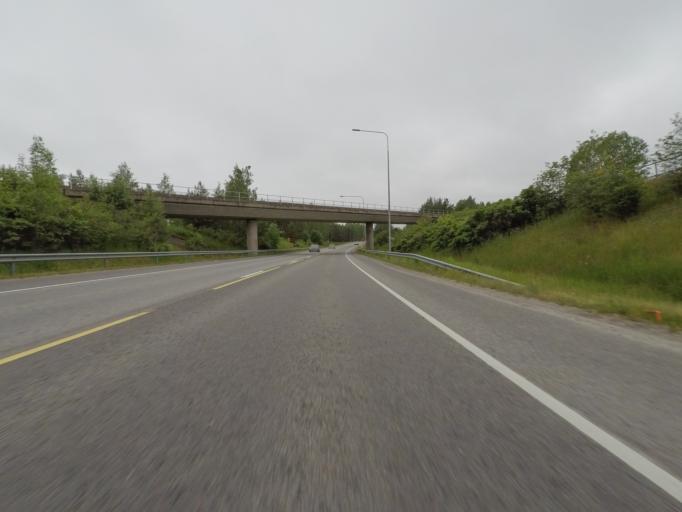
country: FI
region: Varsinais-Suomi
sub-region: Turku
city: Raisio
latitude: 60.4607
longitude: 22.1839
